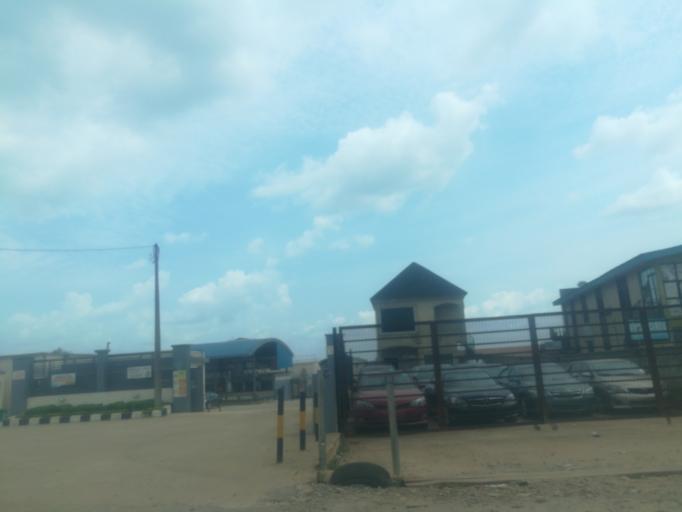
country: NG
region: Oyo
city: Ibadan
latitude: 7.4210
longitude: 3.9356
